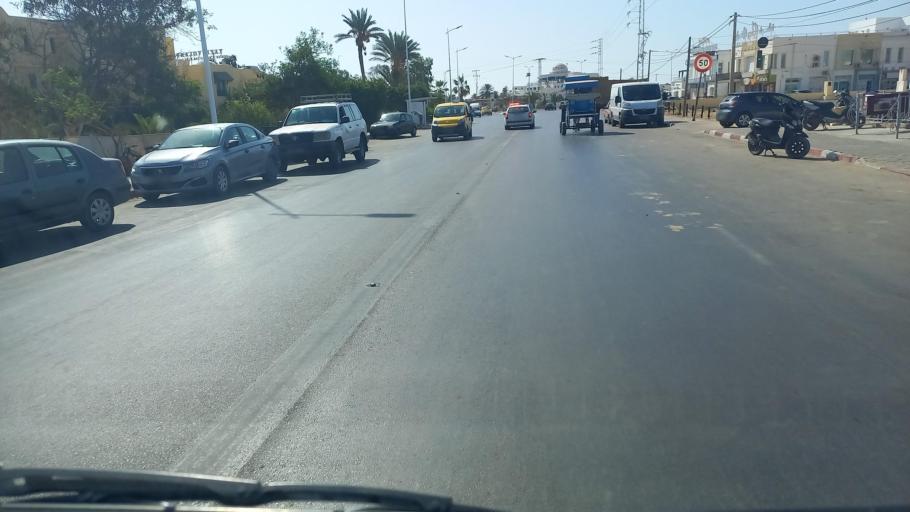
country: TN
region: Madanin
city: Midoun
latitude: 33.8400
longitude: 10.9919
